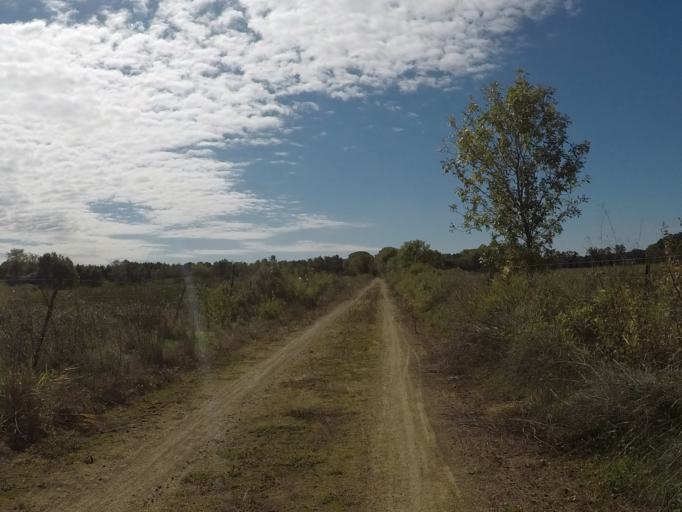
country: US
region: Wisconsin
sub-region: Richland County
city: Richland Center
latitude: 43.2330
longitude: -90.2997
